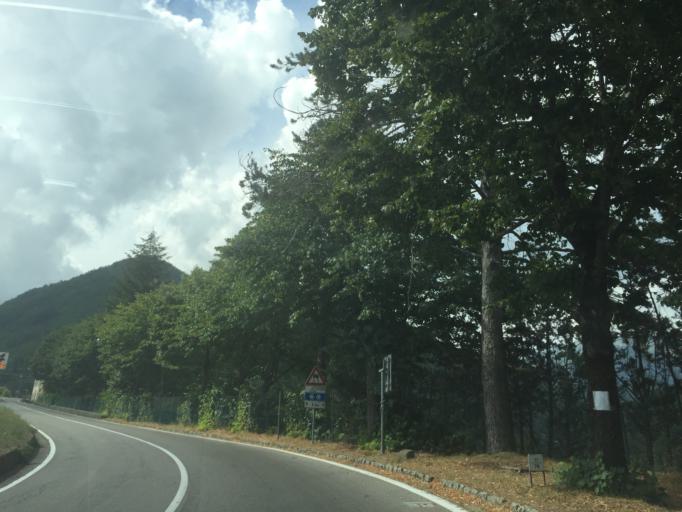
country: IT
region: Tuscany
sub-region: Provincia di Pistoia
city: Cutigliano
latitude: 44.1015
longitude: 10.7478
